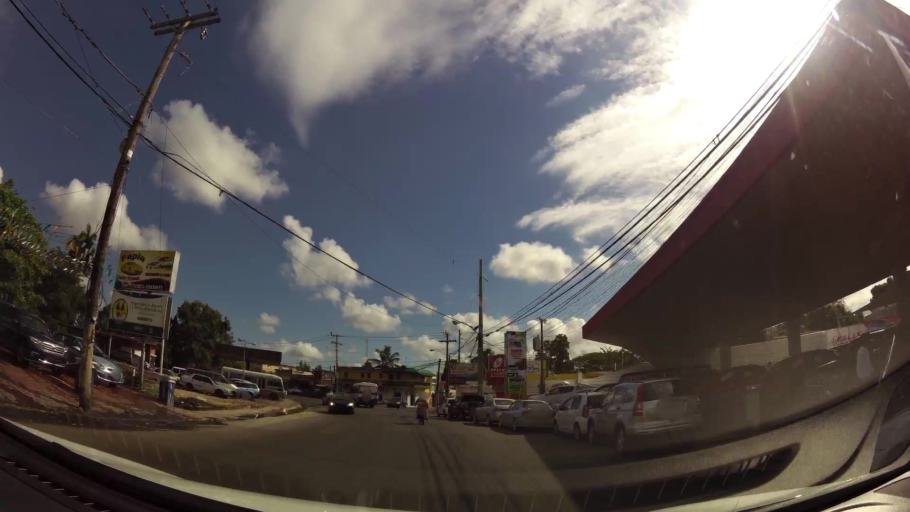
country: DO
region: Santo Domingo
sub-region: Santo Domingo
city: Santo Domingo Este
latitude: 18.4966
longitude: -69.8606
